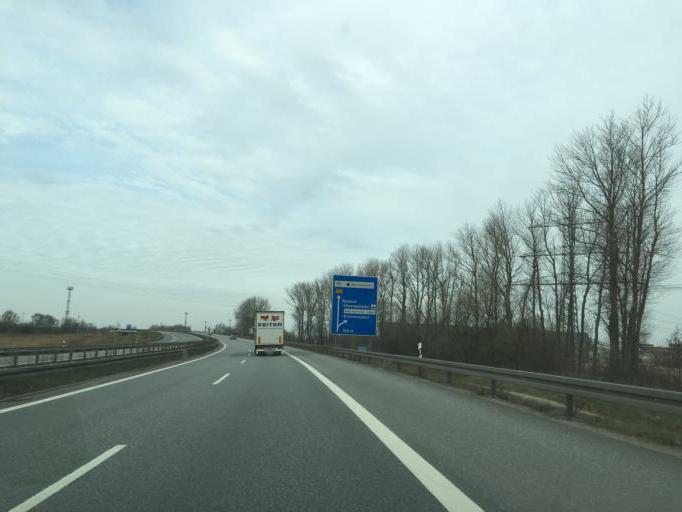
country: DE
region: Mecklenburg-Vorpommern
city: Dierkow-West
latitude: 54.1370
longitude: 12.1327
